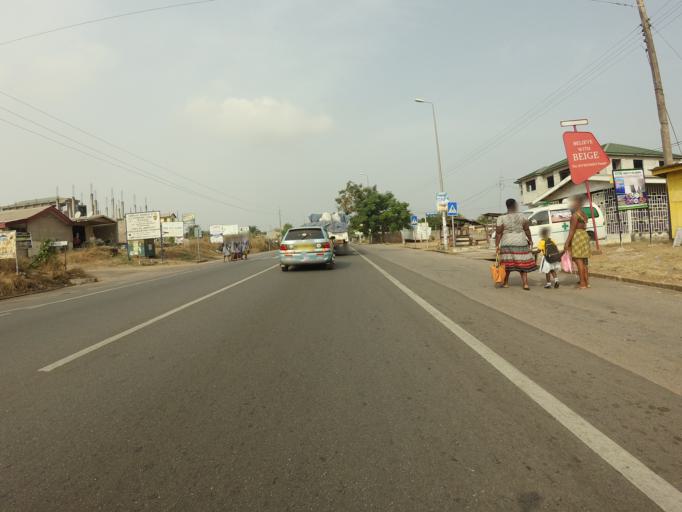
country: GH
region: Volta
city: Ho
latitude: 6.6040
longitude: 0.4806
